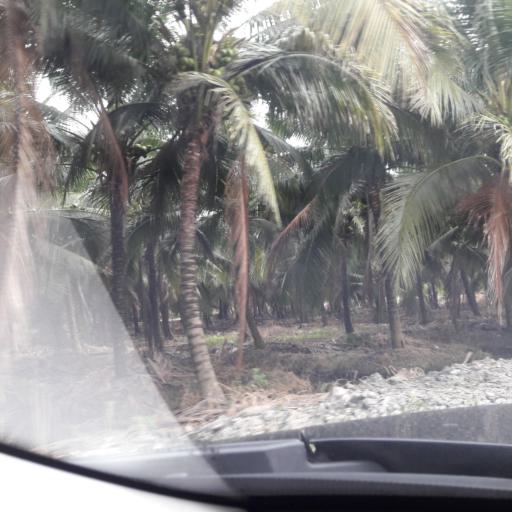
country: TH
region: Ratchaburi
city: Damnoen Saduak
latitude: 13.5843
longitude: 99.9414
